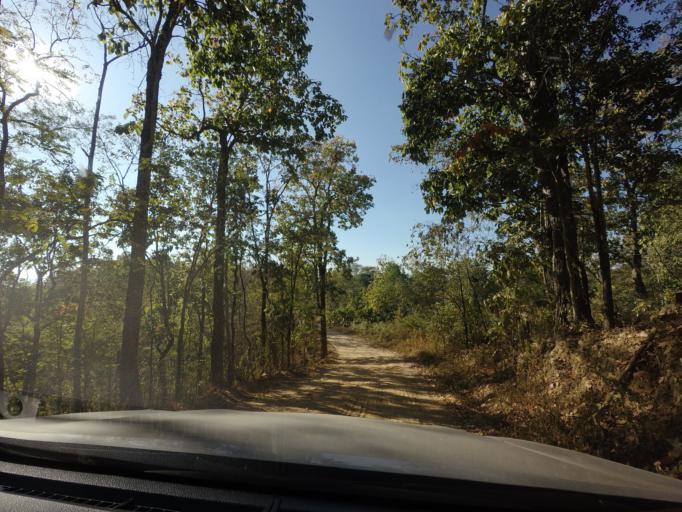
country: TH
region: Lampang
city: Chae Hom
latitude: 18.6153
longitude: 99.6612
